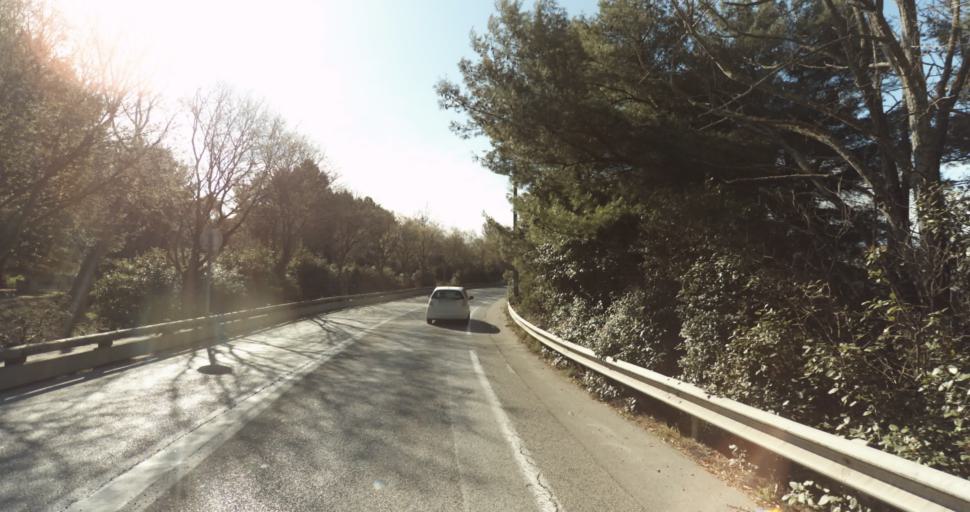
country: FR
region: Provence-Alpes-Cote d'Azur
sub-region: Departement des Bouches-du-Rhone
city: Aix-en-Provence
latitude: 43.5501
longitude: 5.4390
